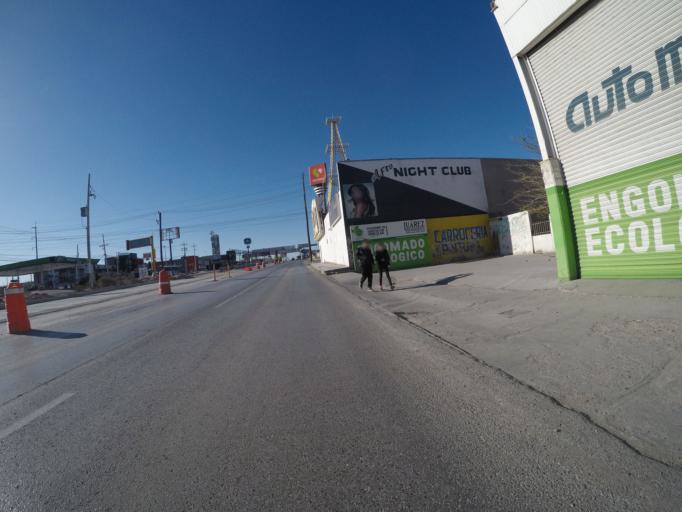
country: MX
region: Chihuahua
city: Ciudad Juarez
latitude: 31.6791
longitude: -106.4248
